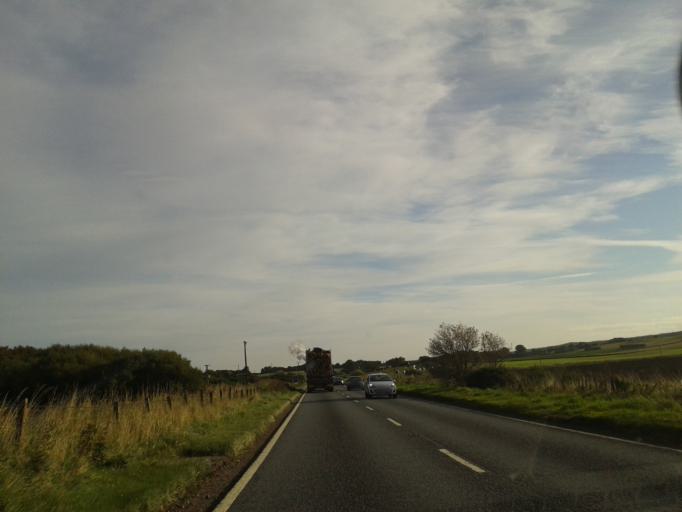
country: GB
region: Scotland
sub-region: Highland
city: Fortrose
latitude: 57.5092
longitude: -4.1090
